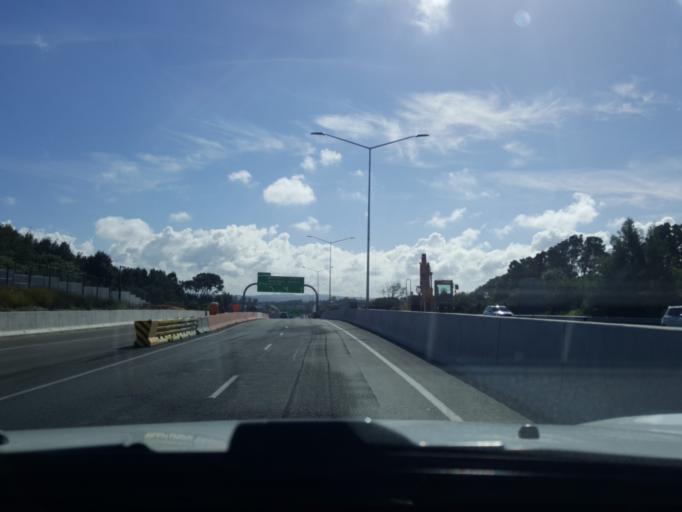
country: NZ
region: Auckland
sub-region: Auckland
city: Rosebank
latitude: -36.8307
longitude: 174.6190
